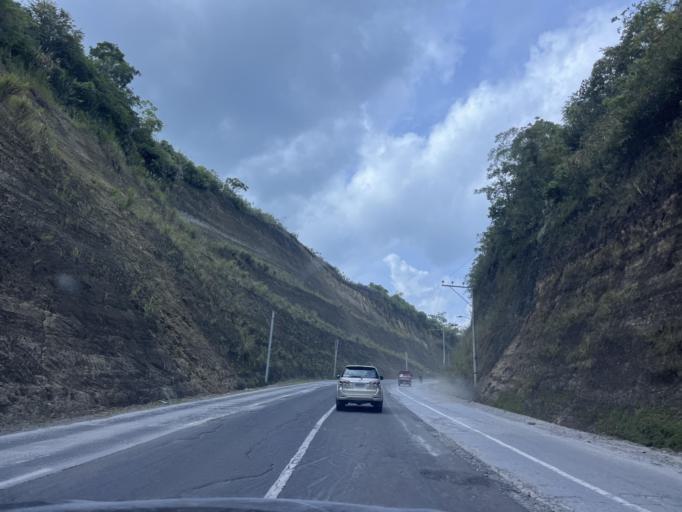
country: PH
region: Davao
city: Simod
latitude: 7.3771
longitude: 125.2780
